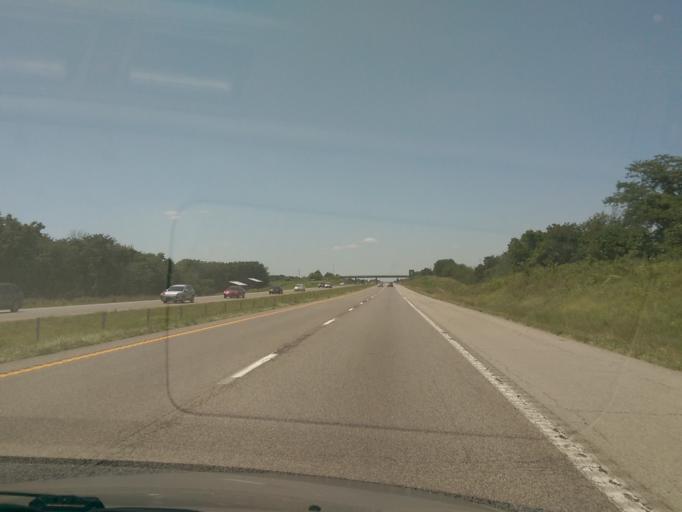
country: US
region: Missouri
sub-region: Saline County
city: Marshall
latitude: 38.9515
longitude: -93.0621
